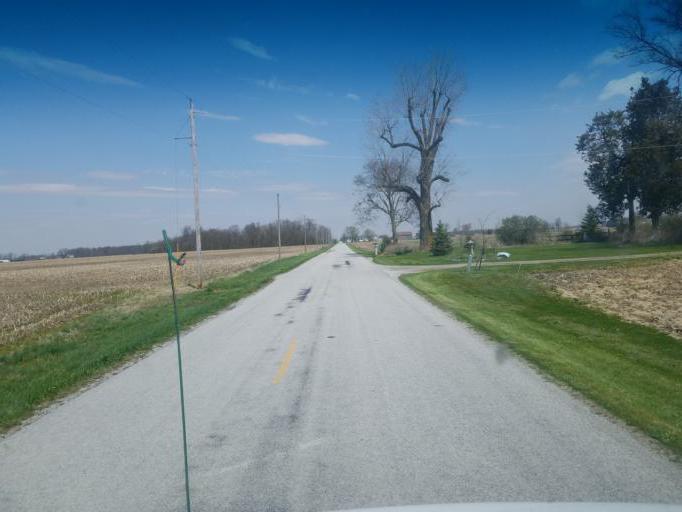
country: US
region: Ohio
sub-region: Hardin County
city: Forest
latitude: 40.7388
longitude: -83.5378
